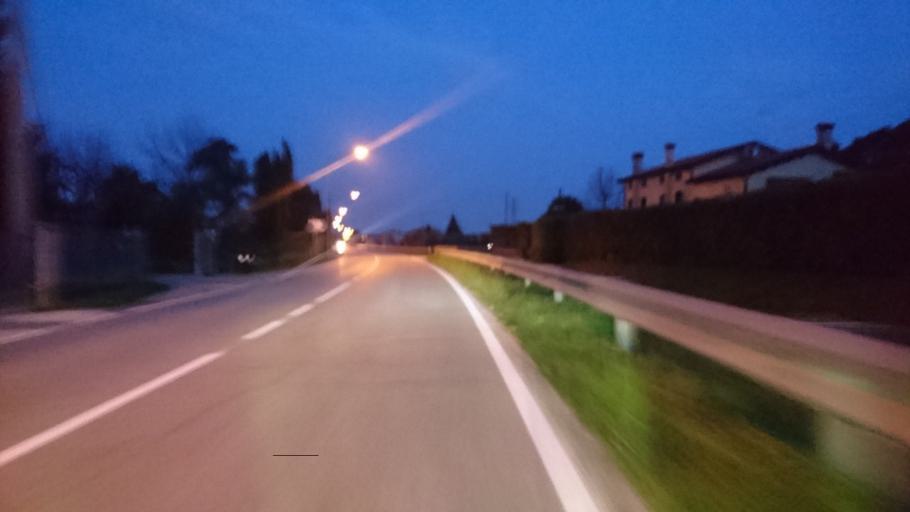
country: IT
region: Veneto
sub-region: Provincia di Padova
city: Selvazzano Dentro
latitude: 45.3711
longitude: 11.8001
